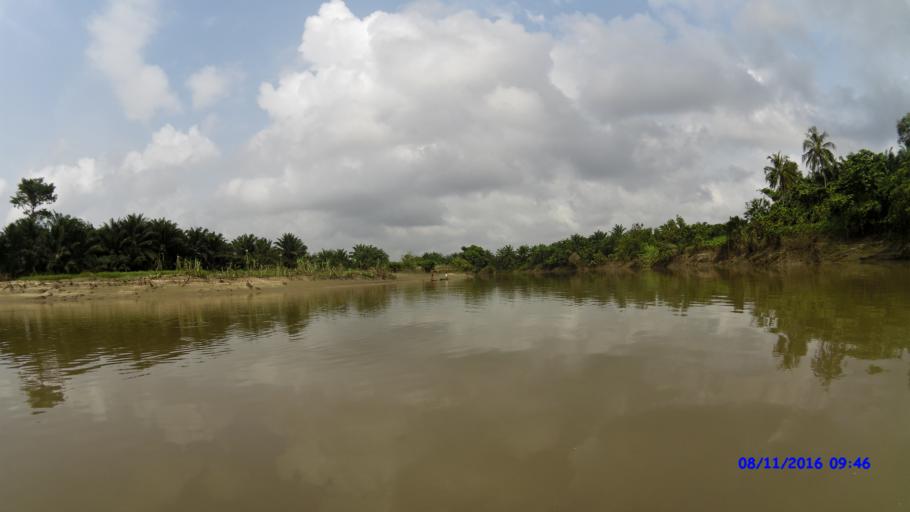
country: BJ
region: Mono
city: Come
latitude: 6.4296
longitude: 1.7734
